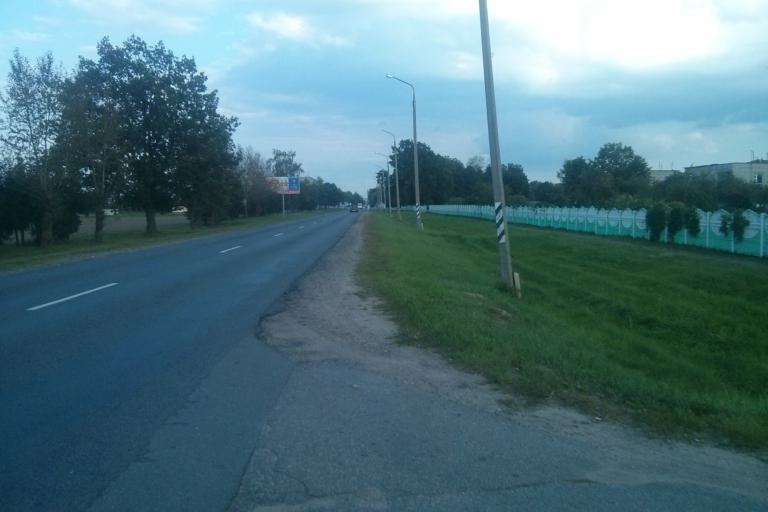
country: BY
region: Minsk
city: Chervyen'
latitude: 53.7206
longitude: 28.3926
